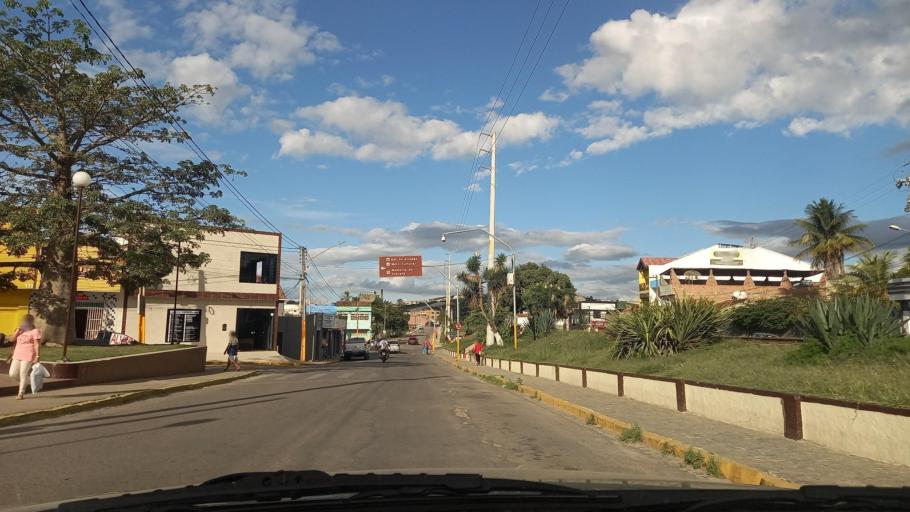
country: BR
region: Pernambuco
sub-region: Gravata
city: Gravata
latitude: -8.2050
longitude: -35.5679
